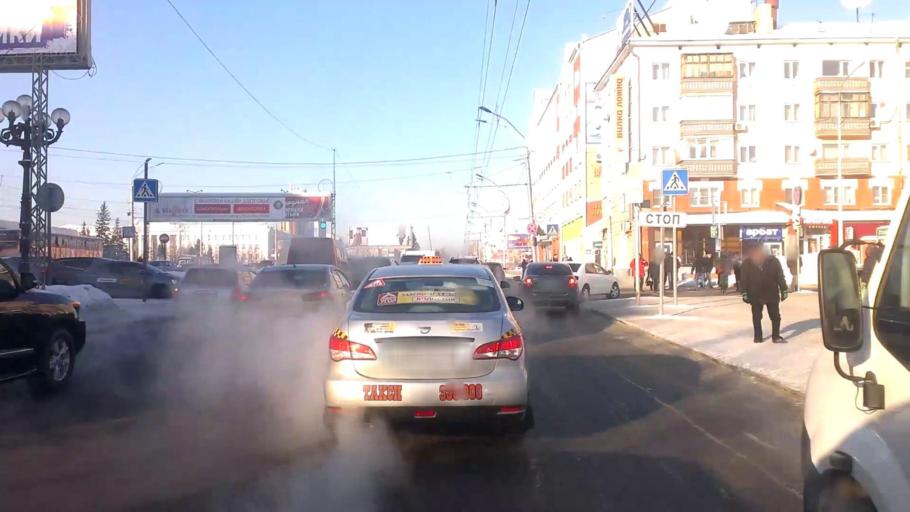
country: RU
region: Altai Krai
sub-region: Gorod Barnaulskiy
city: Barnaul
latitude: 53.3456
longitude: 83.7799
